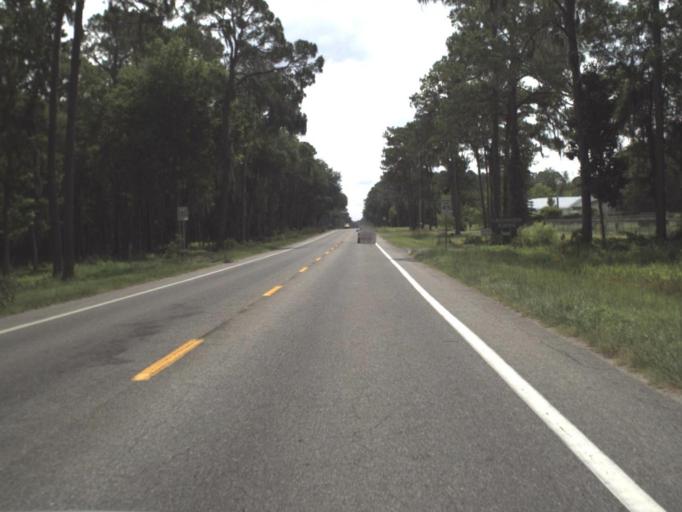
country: US
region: Florida
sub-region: Hamilton County
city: Jasper
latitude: 30.5242
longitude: -82.9856
